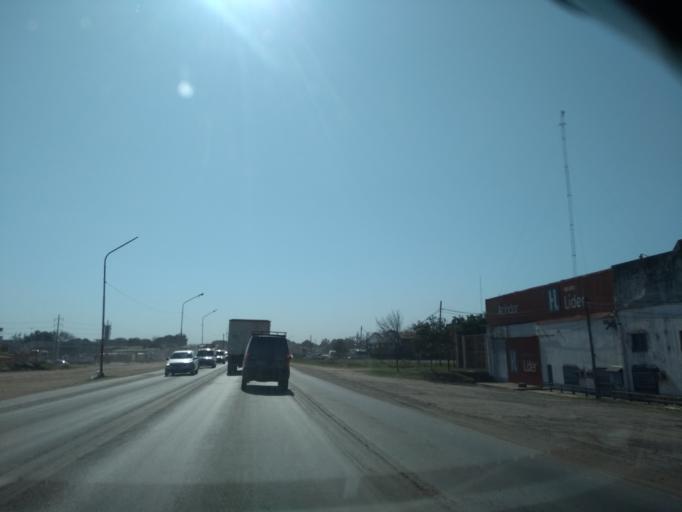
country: AR
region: Chaco
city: Fontana
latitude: -27.4247
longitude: -59.0093
